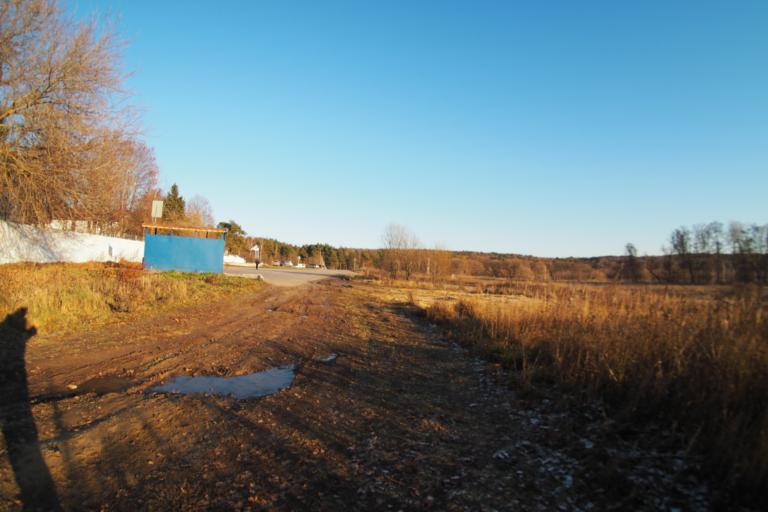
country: RU
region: Moskovskaya
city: Domodedovo
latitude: 55.3845
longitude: 37.7443
